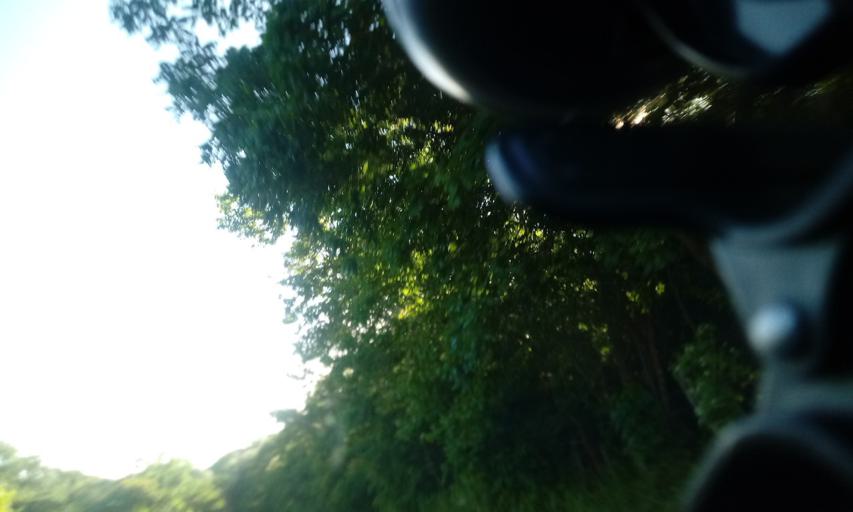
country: BR
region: Bahia
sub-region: Riacho De Santana
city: Riacho de Santana
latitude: -13.8532
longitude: -42.7710
